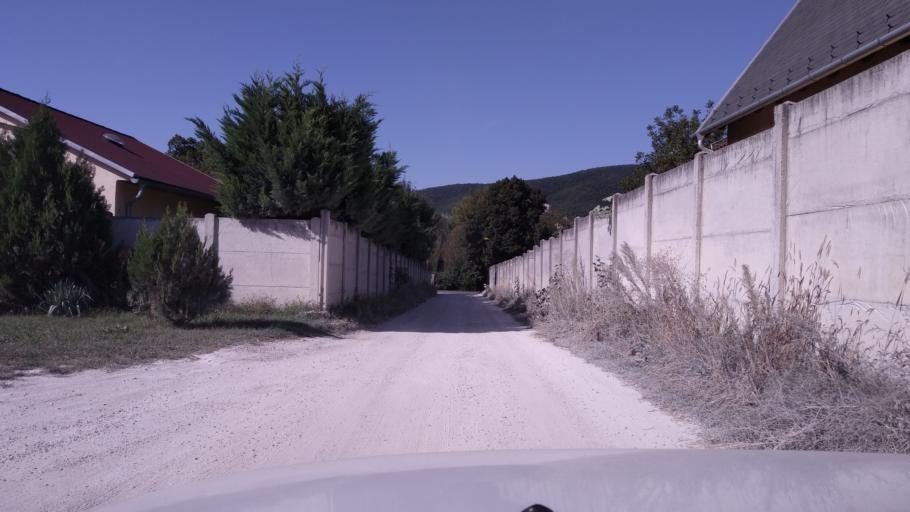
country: HU
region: Komarom-Esztergom
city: Esztergom
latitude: 47.8134
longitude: 18.7858
